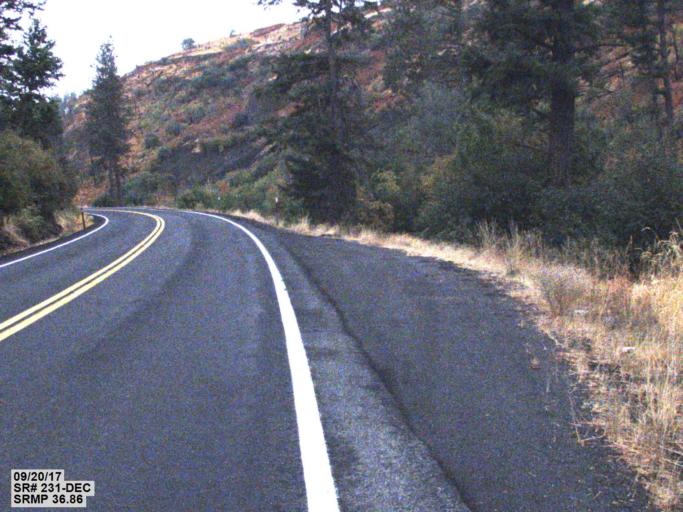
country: US
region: Washington
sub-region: Spokane County
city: Medical Lake
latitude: 47.7458
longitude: -117.8867
